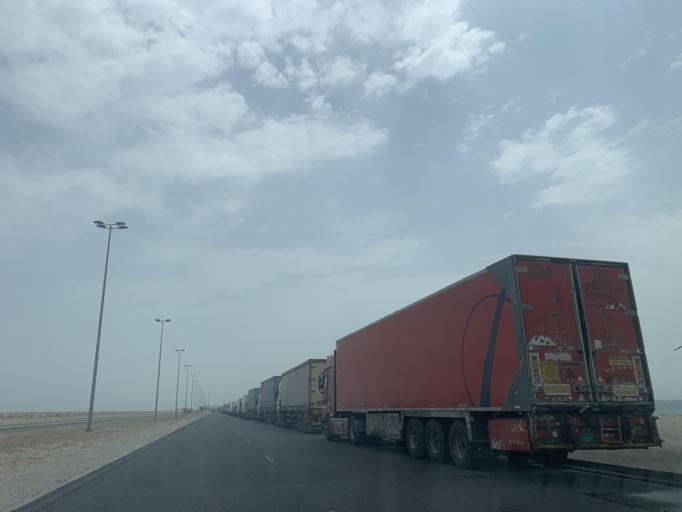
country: BH
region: Muharraq
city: Al Hadd
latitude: 26.2042
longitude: 50.7077
